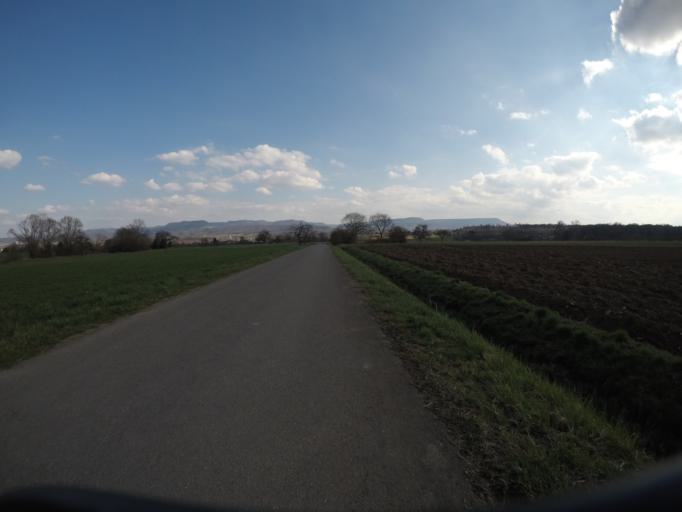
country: DE
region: Baden-Wuerttemberg
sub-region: Tuebingen Region
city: Dusslingen
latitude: 48.4521
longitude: 9.0307
